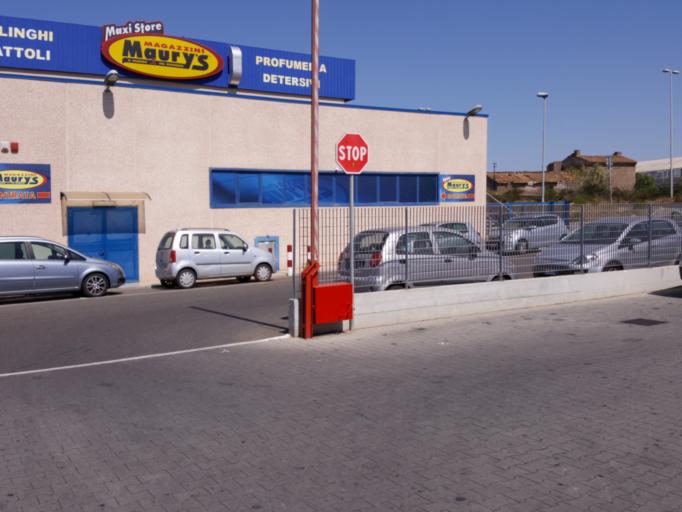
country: IT
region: Latium
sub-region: Citta metropolitana di Roma Capitale
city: Civitavecchia
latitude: 42.1071
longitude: 11.7876
